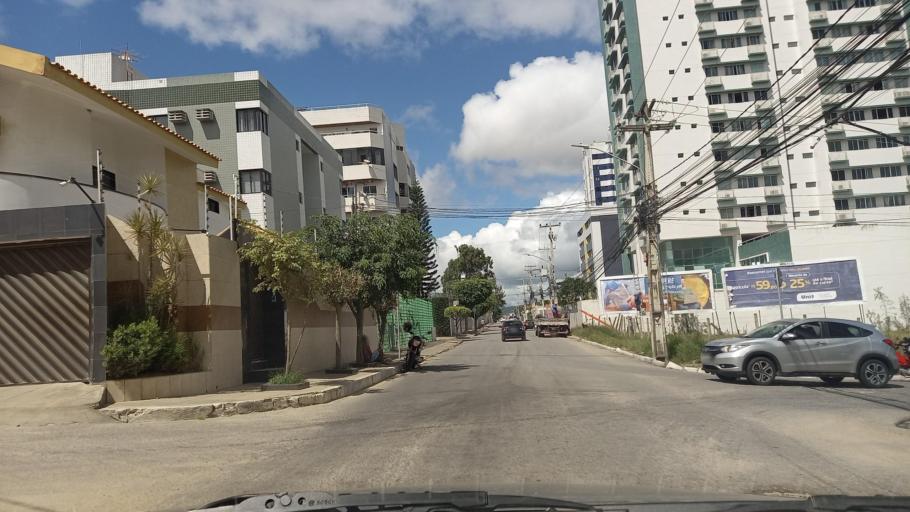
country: BR
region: Pernambuco
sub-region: Caruaru
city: Caruaru
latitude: -8.2656
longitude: -35.9663
